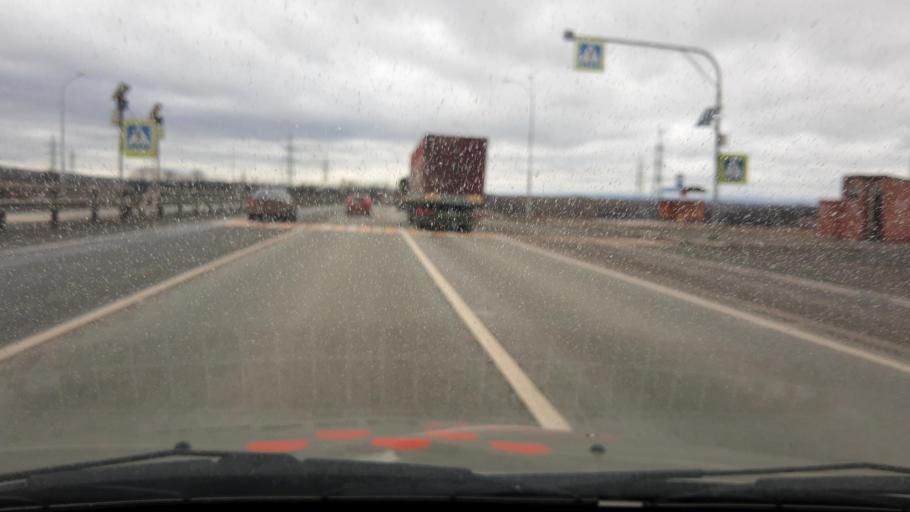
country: RU
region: Bashkortostan
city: Kabakovo
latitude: 54.6537
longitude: 56.1134
